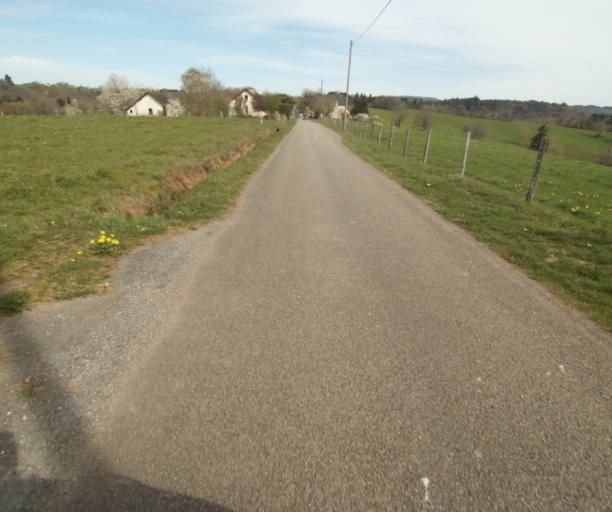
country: FR
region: Limousin
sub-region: Departement de la Correze
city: Correze
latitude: 45.3743
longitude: 1.8199
